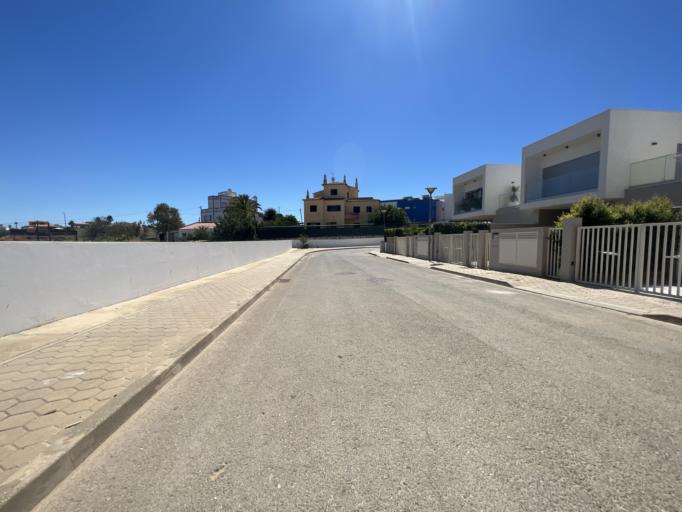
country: PT
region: Faro
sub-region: Portimao
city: Portimao
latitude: 37.1303
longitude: -8.5117
